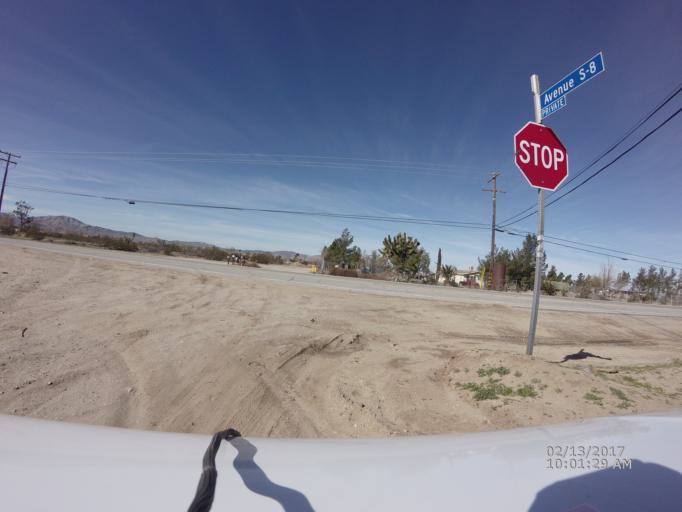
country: US
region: California
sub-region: Los Angeles County
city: Littlerock
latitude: 34.5503
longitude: -117.9746
